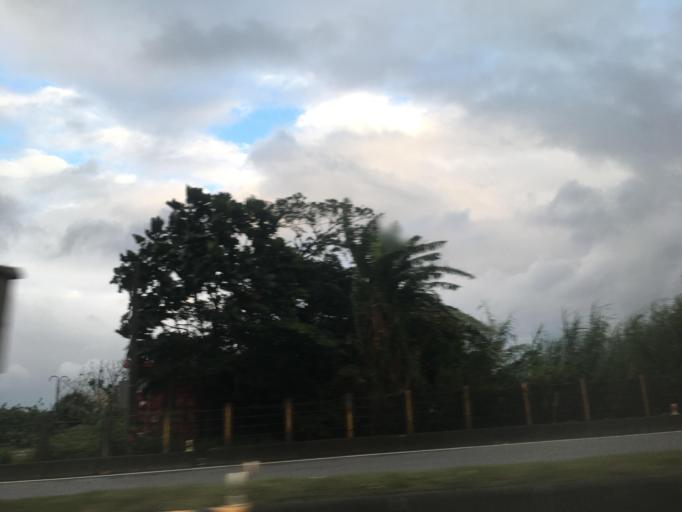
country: TW
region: Taiwan
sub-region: Yilan
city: Yilan
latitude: 24.9219
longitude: 121.8833
